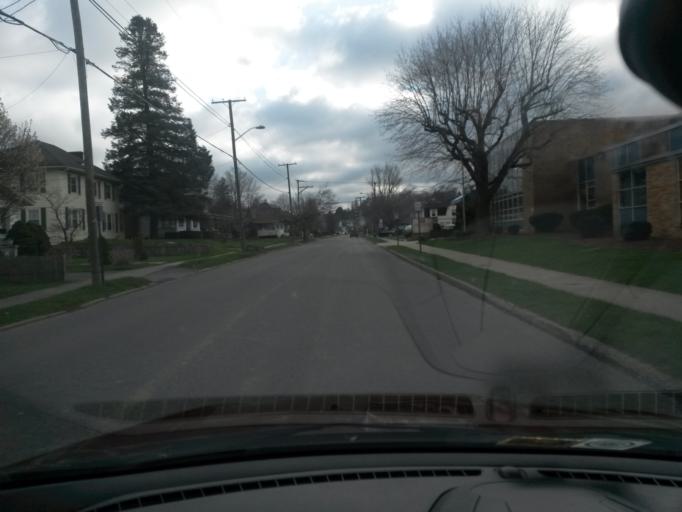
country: US
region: West Virginia
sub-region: Mercer County
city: Bluefield
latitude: 37.2529
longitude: -81.2256
